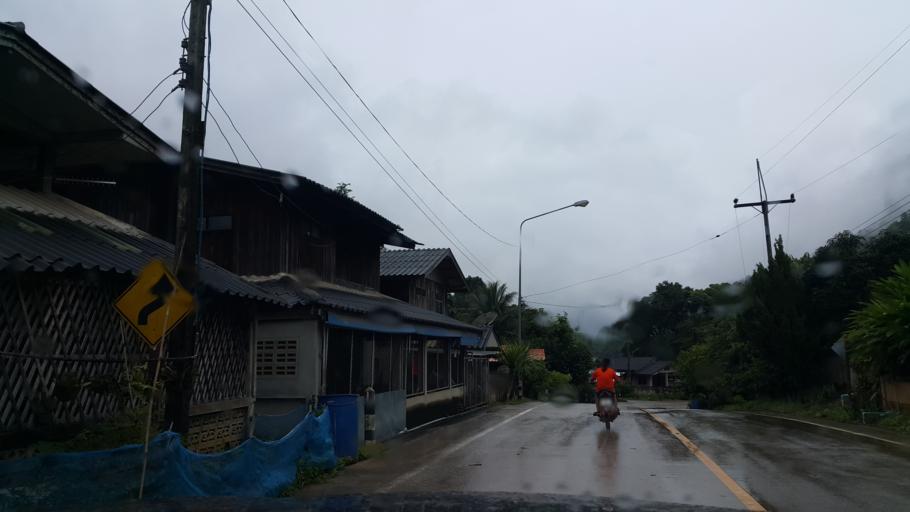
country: TH
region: Phayao
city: Chiang Kham
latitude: 19.5003
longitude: 100.4568
